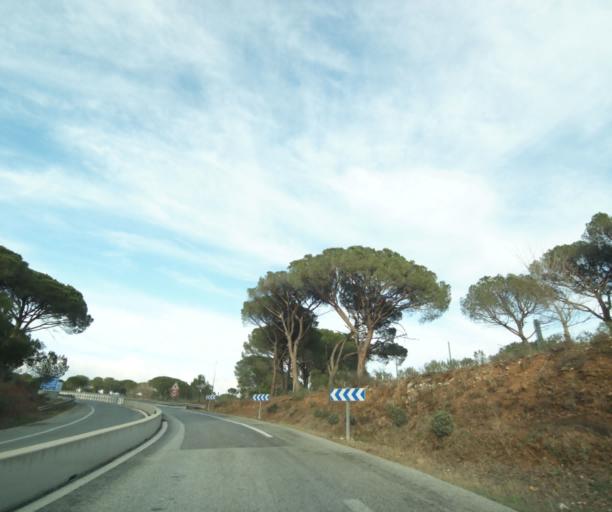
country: FR
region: Provence-Alpes-Cote d'Azur
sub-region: Departement du Var
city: Le Muy
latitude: 43.4580
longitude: 6.5536
